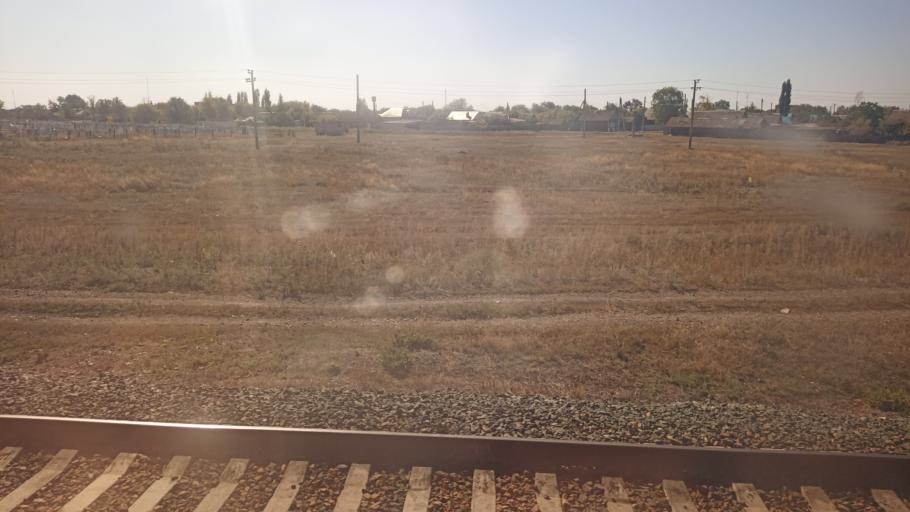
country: RU
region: Saratov
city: Pushkino
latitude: 51.2320
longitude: 46.9854
